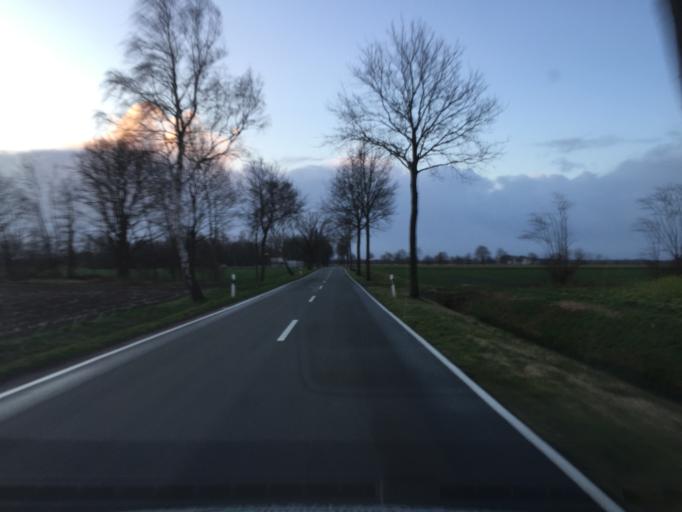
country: DE
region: Lower Saxony
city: Maasen
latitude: 52.6744
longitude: 8.8913
